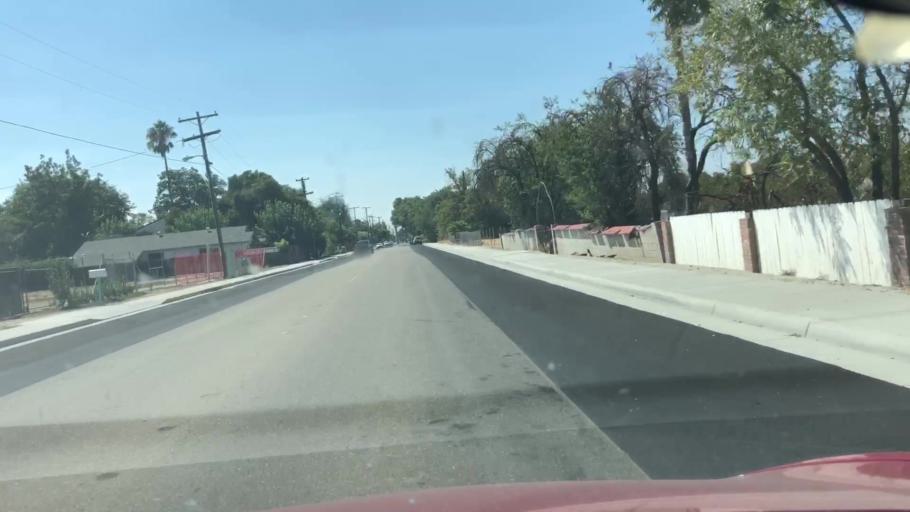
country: US
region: California
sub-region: San Joaquin County
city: Tracy
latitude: 37.7289
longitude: -121.4274
